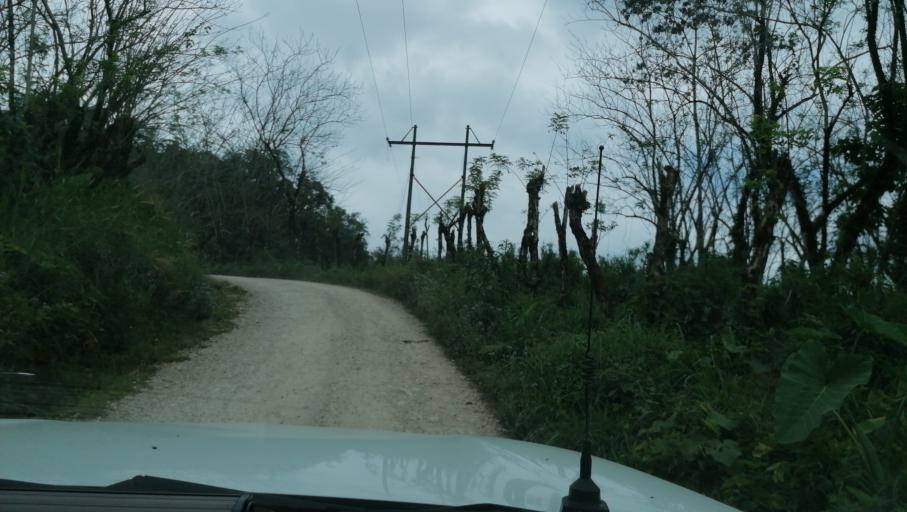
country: MX
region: Chiapas
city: Ocotepec
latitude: 17.2761
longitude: -93.2258
